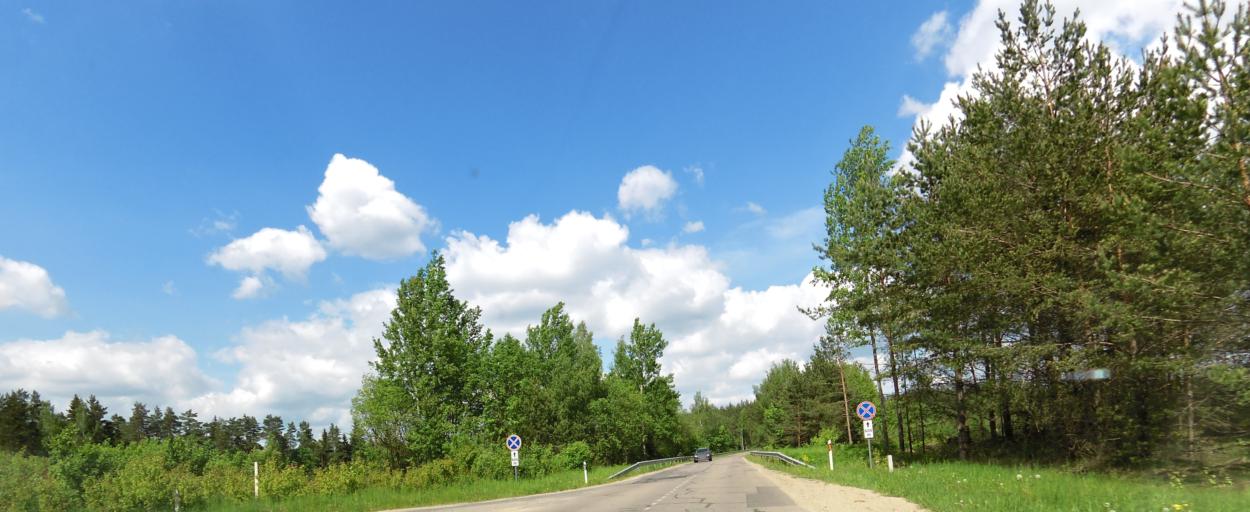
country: LT
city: Trakai
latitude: 54.7124
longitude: 24.9728
